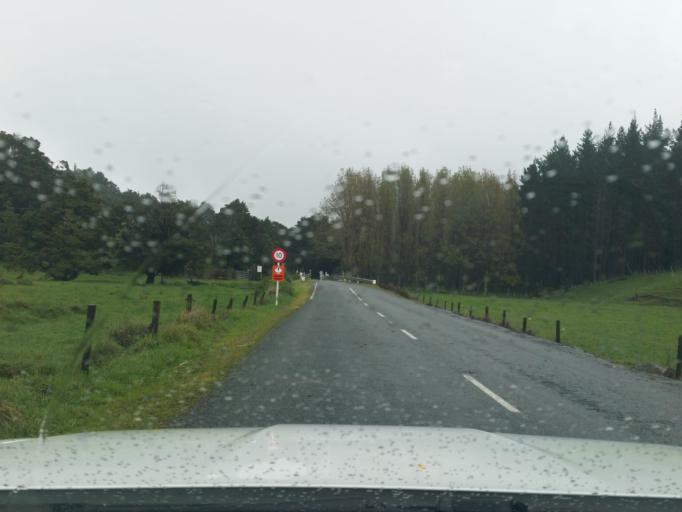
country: NZ
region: Northland
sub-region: Kaipara District
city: Dargaville
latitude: -35.8076
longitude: 173.9982
